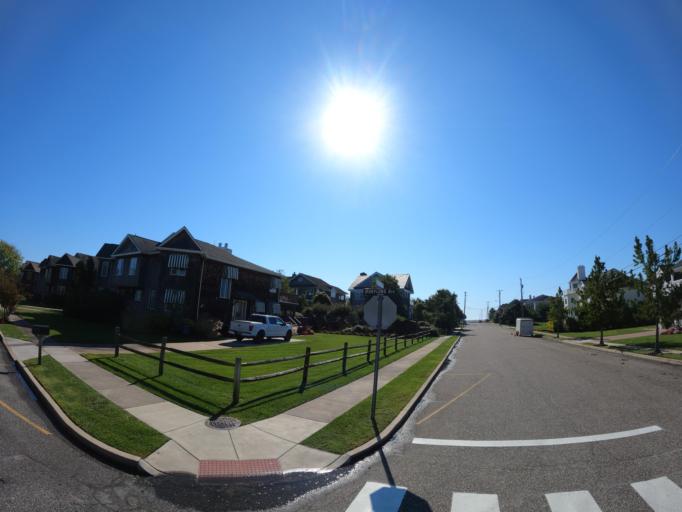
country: US
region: New Jersey
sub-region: Cape May County
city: Cape May
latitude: 38.9392
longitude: -74.8951
